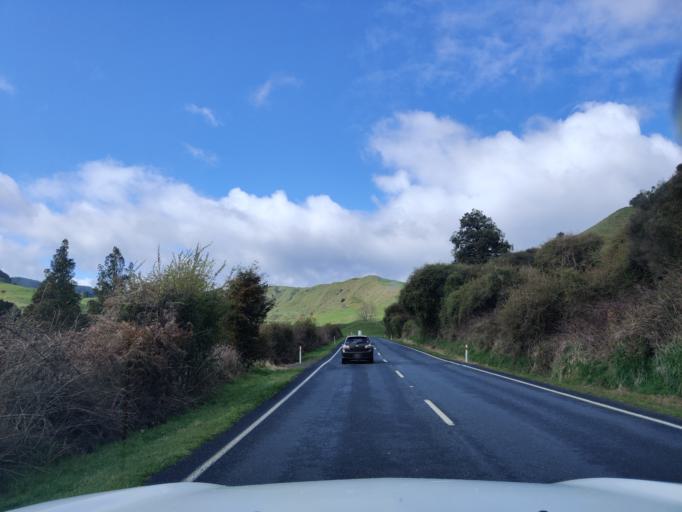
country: NZ
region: Waikato
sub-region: Otorohanga District
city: Otorohanga
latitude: -38.5915
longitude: 175.2183
